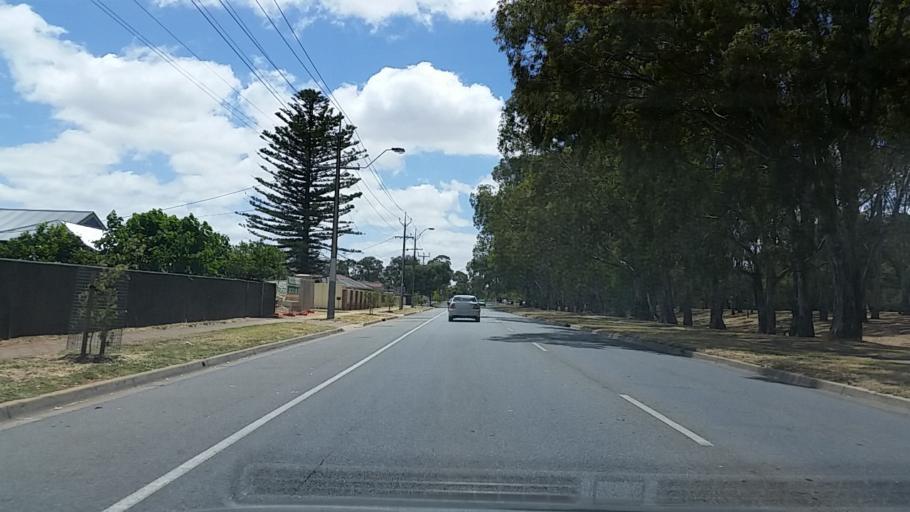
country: AU
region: South Australia
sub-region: Salisbury
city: Salisbury
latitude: -34.7705
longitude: 138.6183
